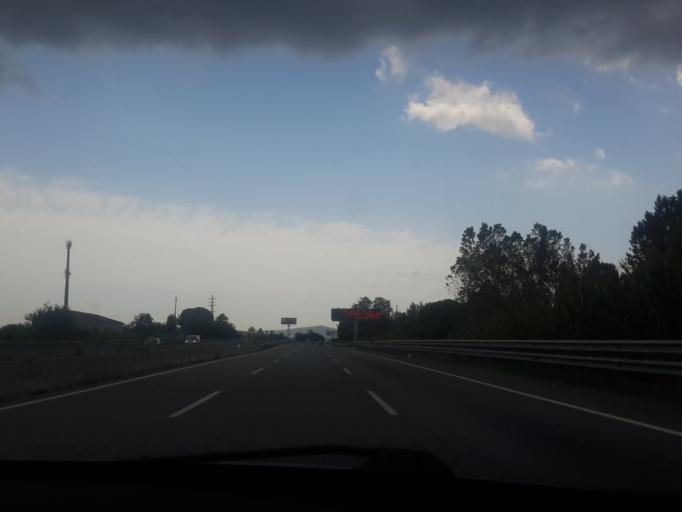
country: ES
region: Catalonia
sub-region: Provincia de Girona
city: Sils
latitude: 41.8145
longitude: 2.7469
